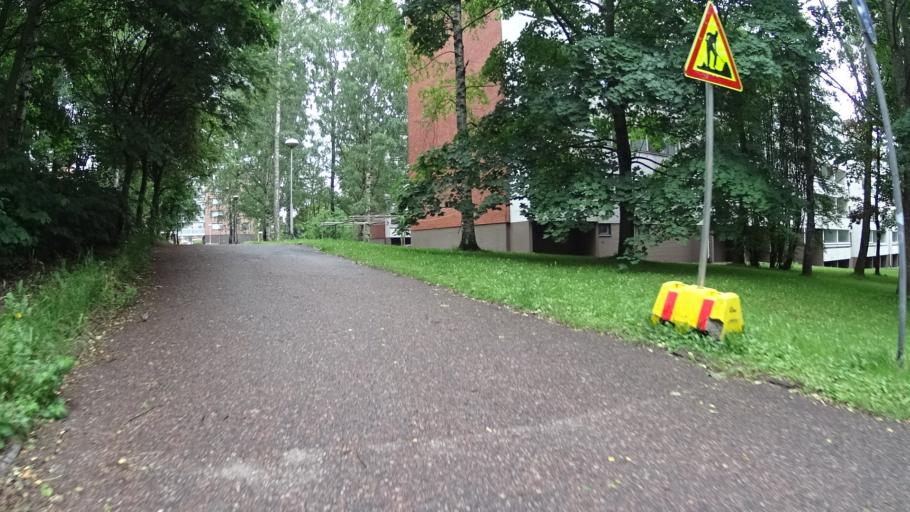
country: FI
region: Uusimaa
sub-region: Helsinki
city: Teekkarikylae
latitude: 60.2649
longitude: 24.8430
